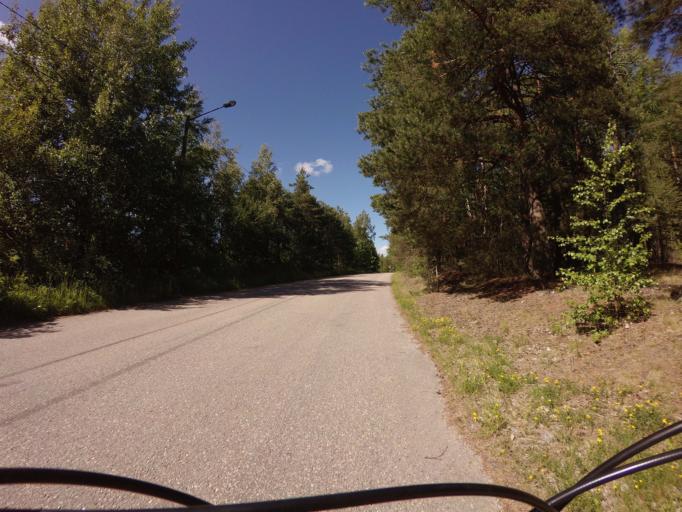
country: FI
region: Varsinais-Suomi
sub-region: Turku
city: Turku
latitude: 60.4943
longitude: 22.2794
